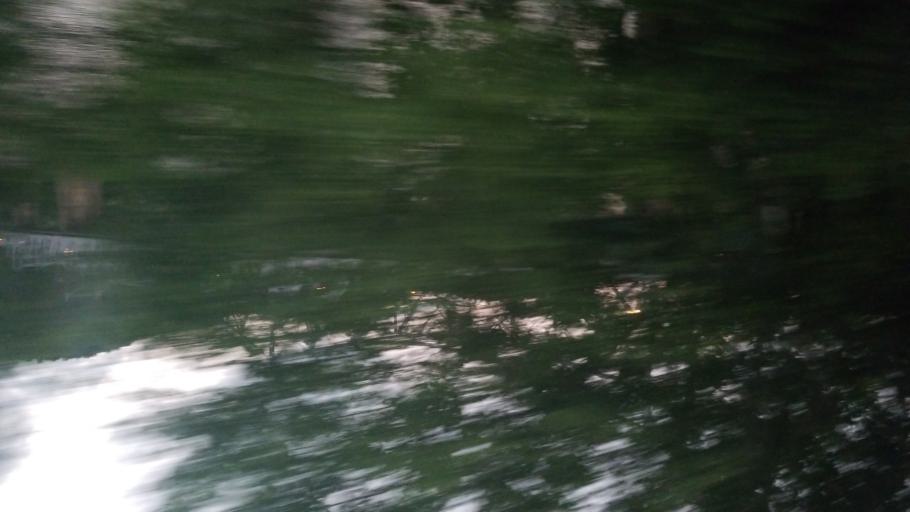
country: US
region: Pennsylvania
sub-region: Beaver County
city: Ambridge
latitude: 40.5931
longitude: -80.2341
